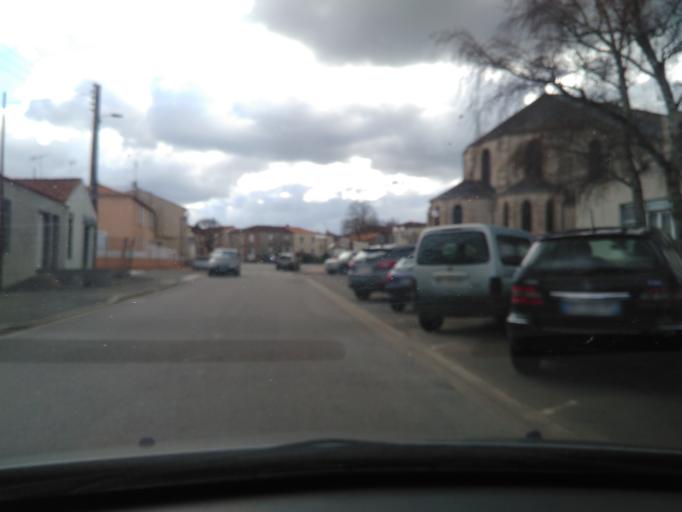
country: FR
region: Pays de la Loire
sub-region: Departement de la Vendee
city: Saint-Martin-des-Noyers
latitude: 46.7219
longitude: -1.1775
